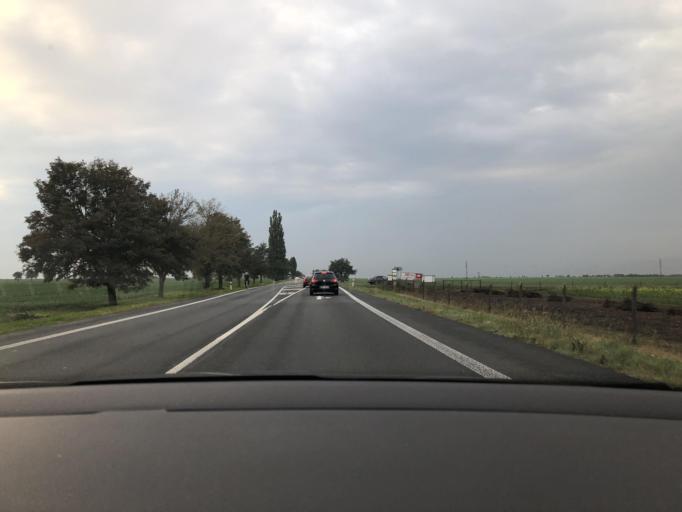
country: CZ
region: Central Bohemia
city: Velim
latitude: 50.0428
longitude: 15.0893
